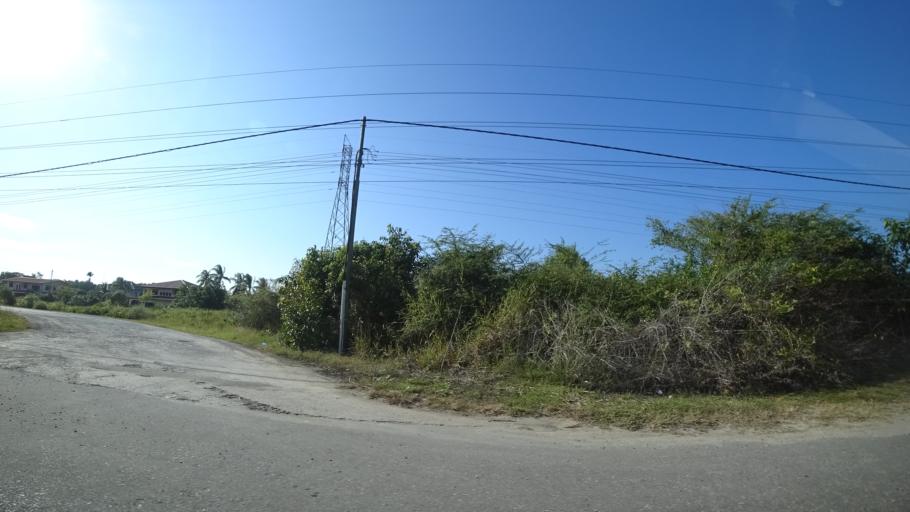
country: BN
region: Tutong
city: Tutong
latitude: 4.7259
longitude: 114.5507
